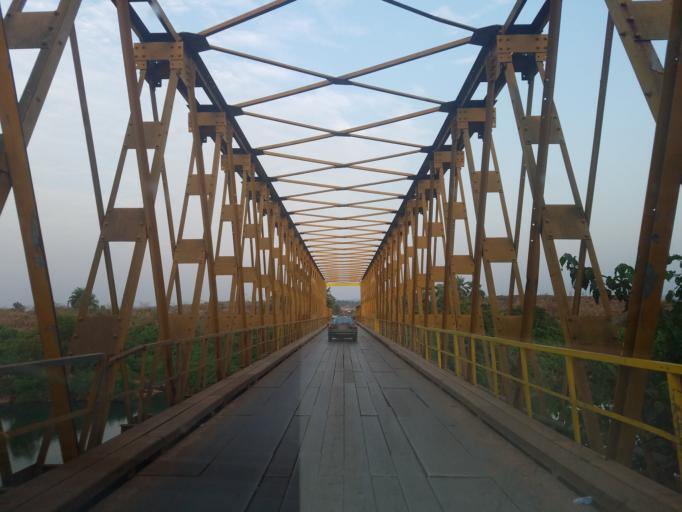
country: GN
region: Boke
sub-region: Fria
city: Fria
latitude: 10.0879
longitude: -13.6730
